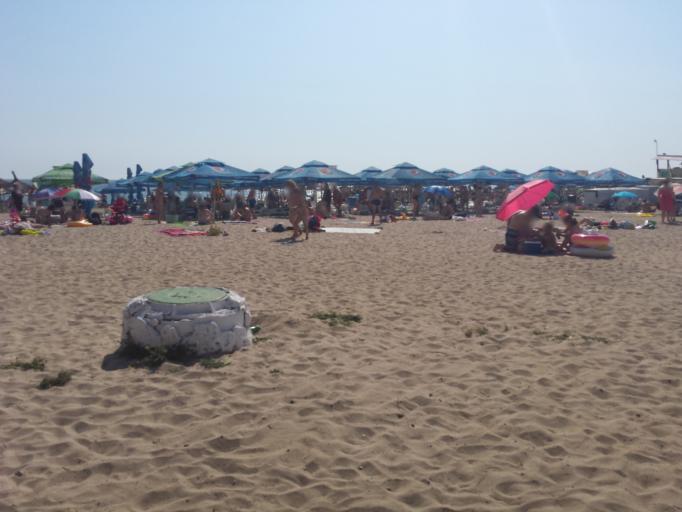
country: RO
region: Constanta
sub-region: Comuna Douazeci si Trei August
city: Douazeci si Trei August
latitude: 43.8598
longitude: 28.6060
